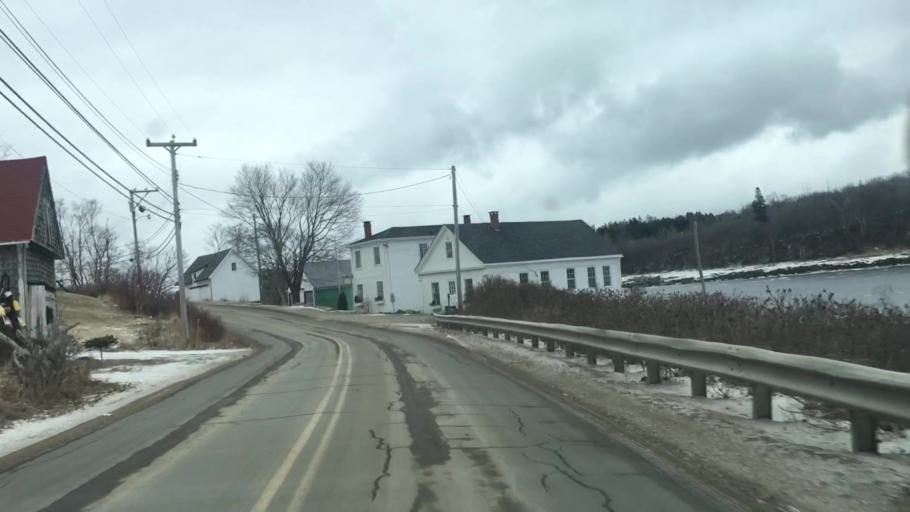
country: US
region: Maine
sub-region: Washington County
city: Machiasport
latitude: 44.6965
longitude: -67.3941
